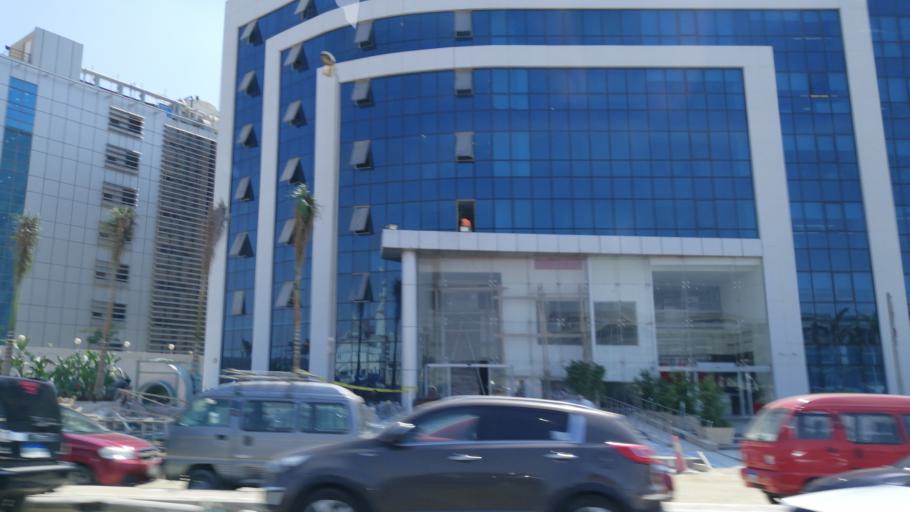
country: EG
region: Muhafazat al Qalyubiyah
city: Al Khankah
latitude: 30.0303
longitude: 31.4668
